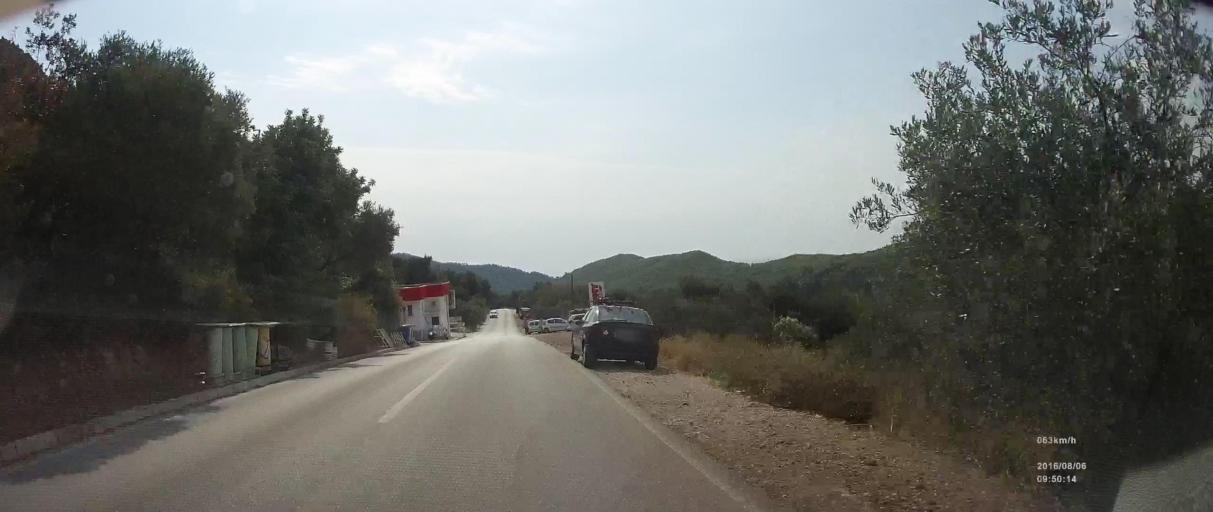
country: HR
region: Dubrovacko-Neretvanska
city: Blato
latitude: 42.7346
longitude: 17.5508
